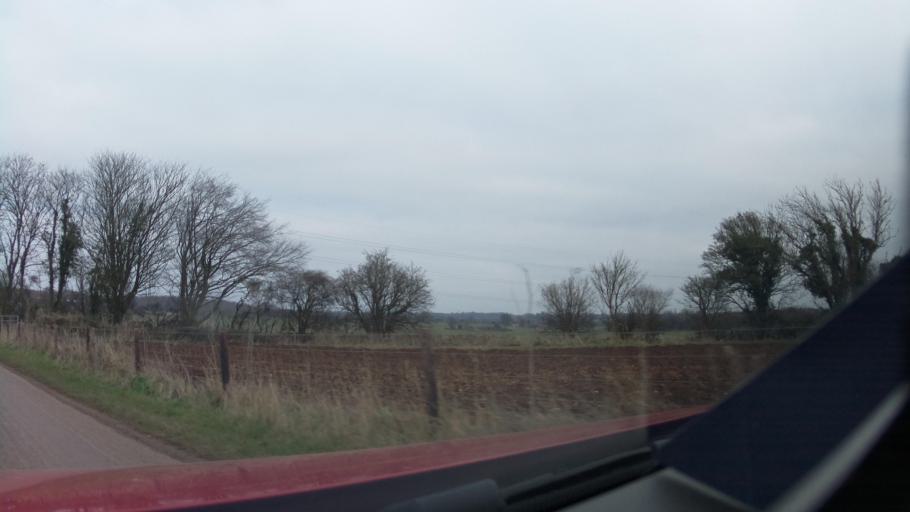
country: GB
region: England
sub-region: Wiltshire
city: Nettleton
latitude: 51.4863
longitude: -2.2816
